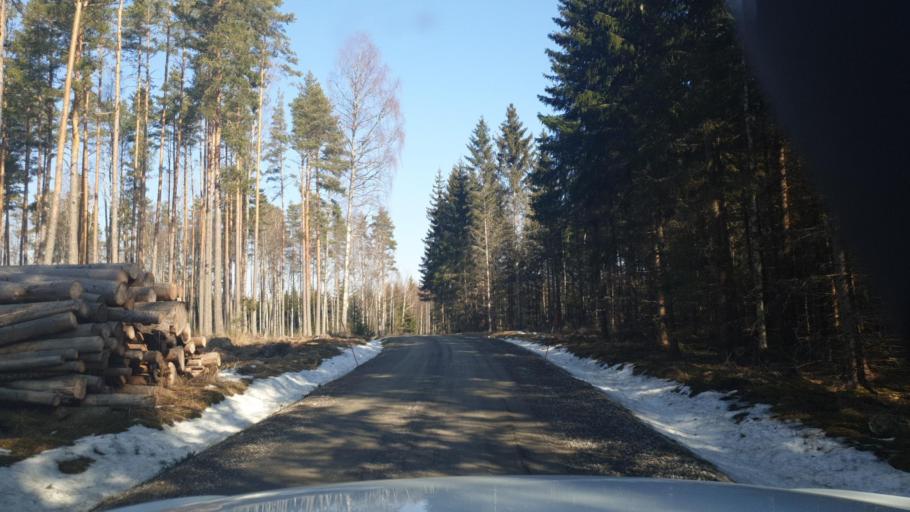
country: SE
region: Vaermland
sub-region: Karlstads Kommun
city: Edsvalla
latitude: 59.4640
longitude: 13.1207
